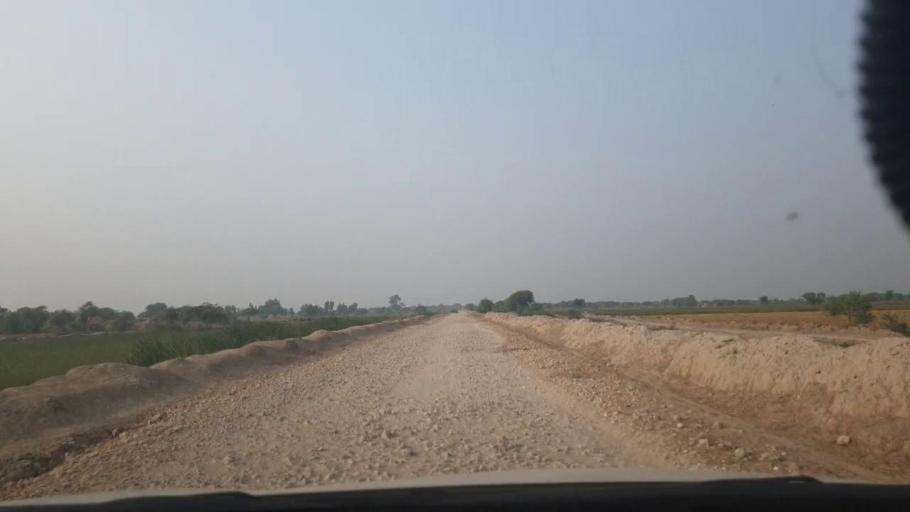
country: PK
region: Sindh
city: Bulri
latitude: 24.7948
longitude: 68.4167
